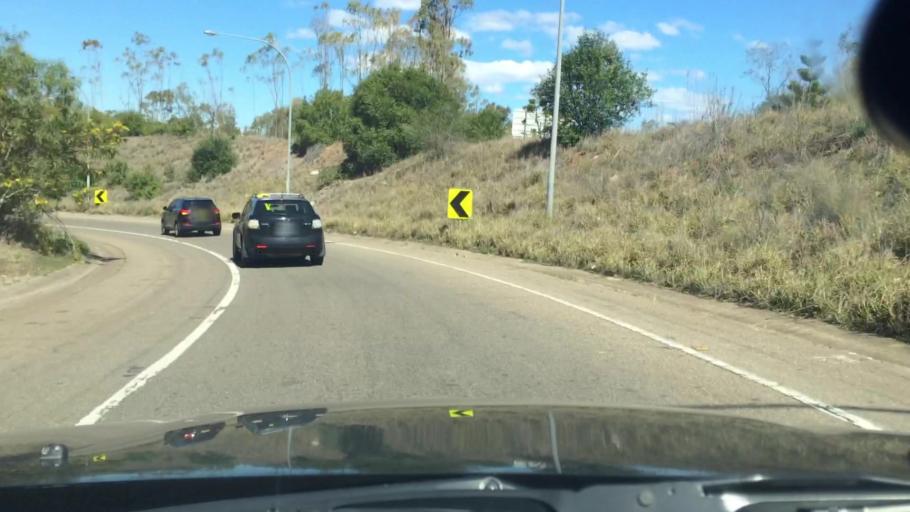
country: AU
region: New South Wales
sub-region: Campbelltown Municipality
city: Glen Alpine
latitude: -34.0621
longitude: 150.7829
